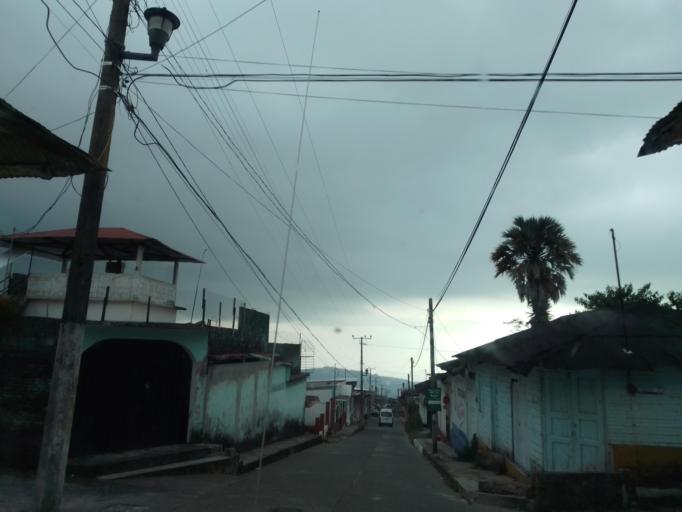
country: MX
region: Chiapas
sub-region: Union Juarez
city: Santo Domingo
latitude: 15.0625
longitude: -92.0813
